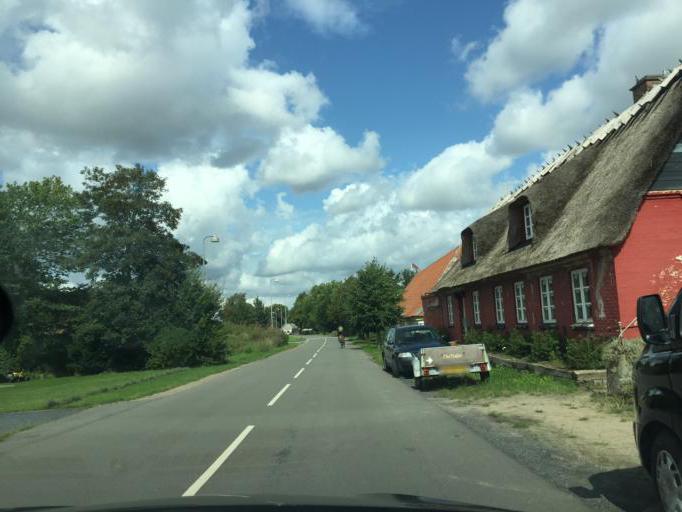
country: DK
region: South Denmark
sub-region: Odense Kommune
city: Stige
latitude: 55.4603
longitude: 10.3772
